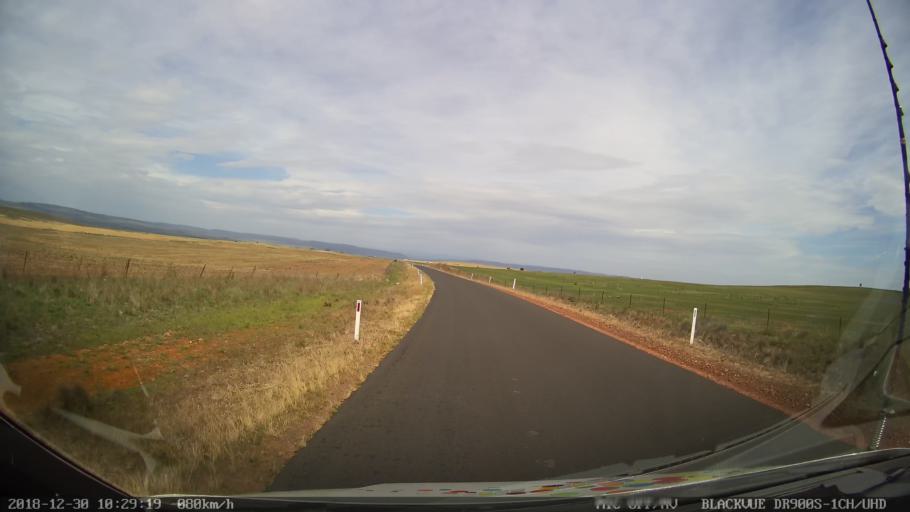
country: AU
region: New South Wales
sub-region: Snowy River
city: Berridale
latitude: -36.5017
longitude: 148.9107
